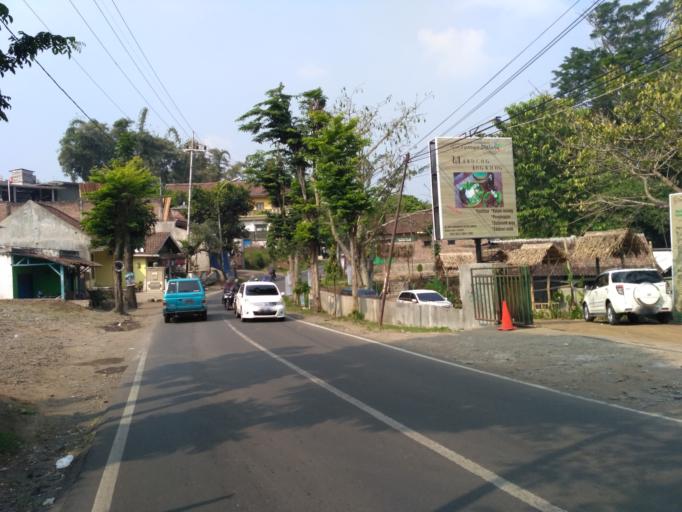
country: ID
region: East Java
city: Batu
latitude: -7.8638
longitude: 112.5538
